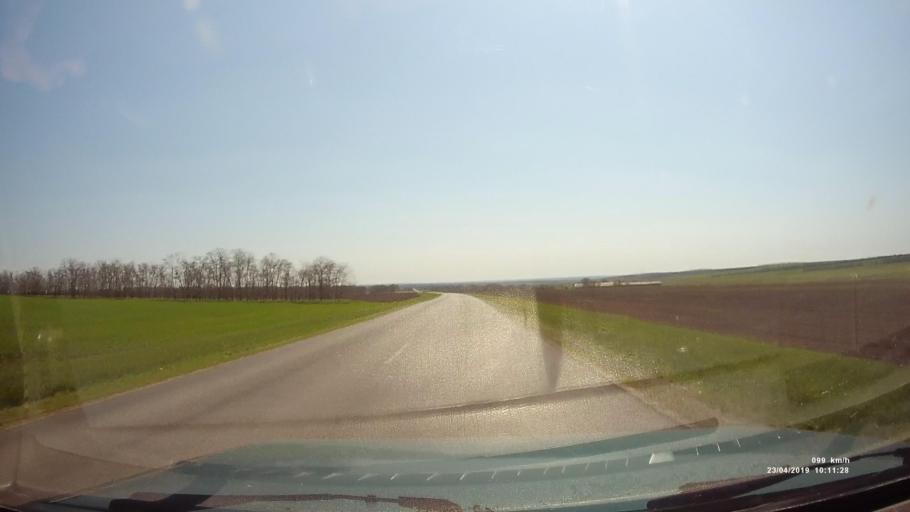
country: RU
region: Rostov
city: Sovetskoye
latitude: 46.6956
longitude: 42.3161
